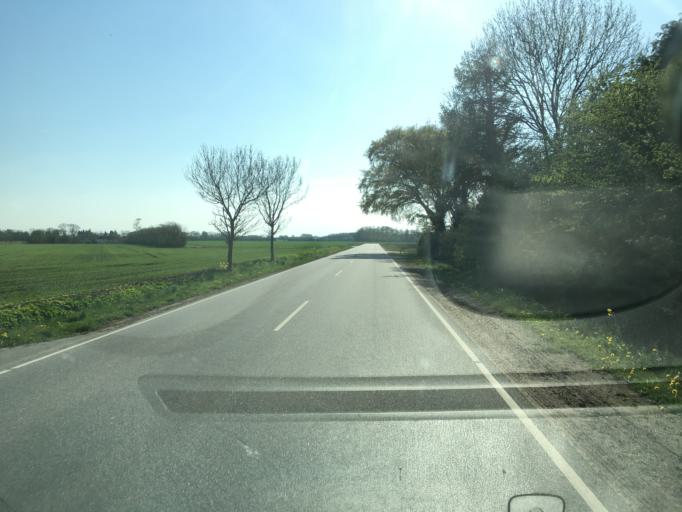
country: DK
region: South Denmark
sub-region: Tonder Kommune
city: Toftlund
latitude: 55.1957
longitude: 9.1180
